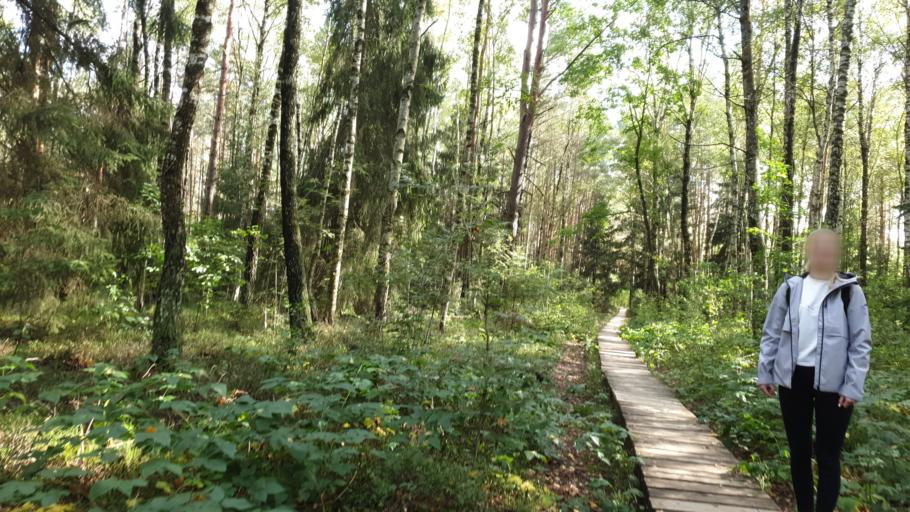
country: LT
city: Trakai
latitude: 54.6391
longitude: 24.9693
